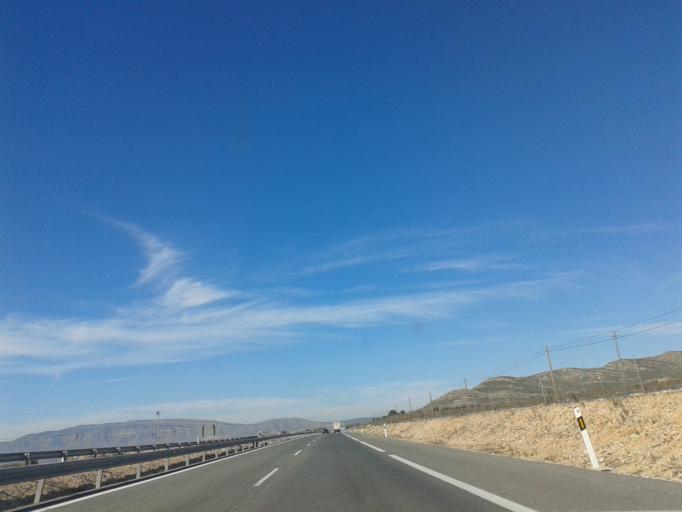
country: ES
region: Valencia
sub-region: Provincia de Alicante
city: Villena
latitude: 38.6826
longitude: -0.9003
